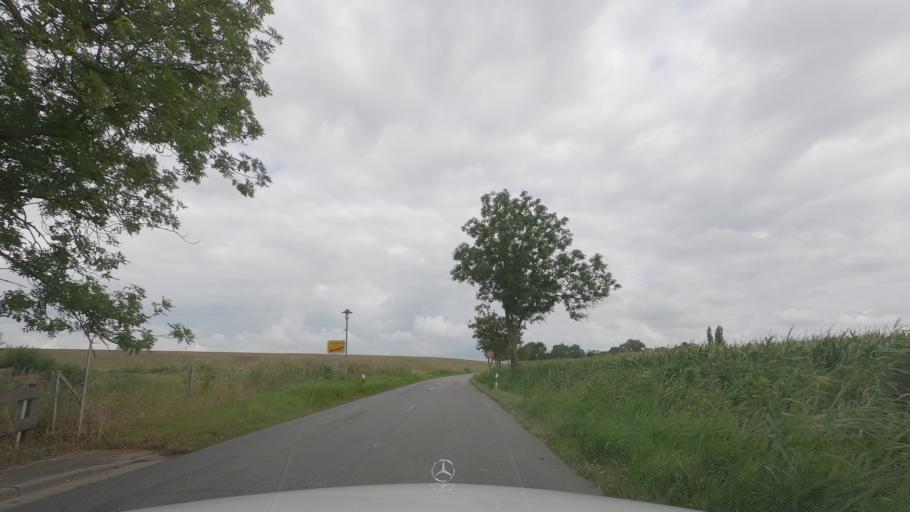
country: DE
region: Lower Saxony
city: Brake (Unterweser)
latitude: 53.2984
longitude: 8.5288
